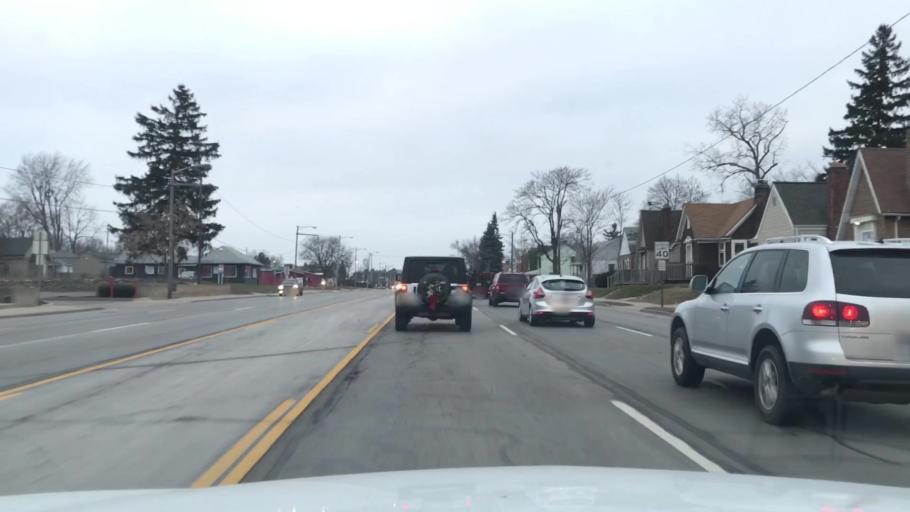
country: US
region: Michigan
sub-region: Oakland County
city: Sylvan Lake
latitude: 42.6366
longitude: -83.3257
